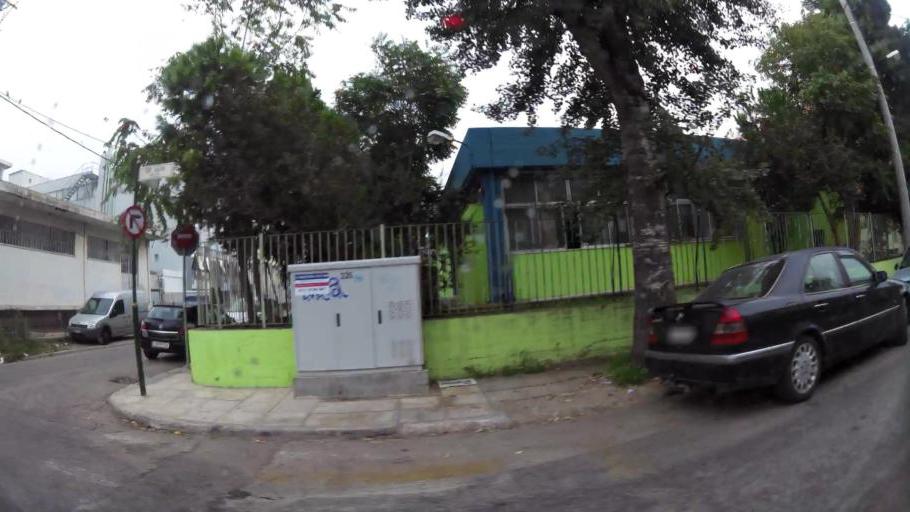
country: GR
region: Attica
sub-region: Nomarchia Athinas
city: Peristeri
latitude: 38.0088
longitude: 23.7090
